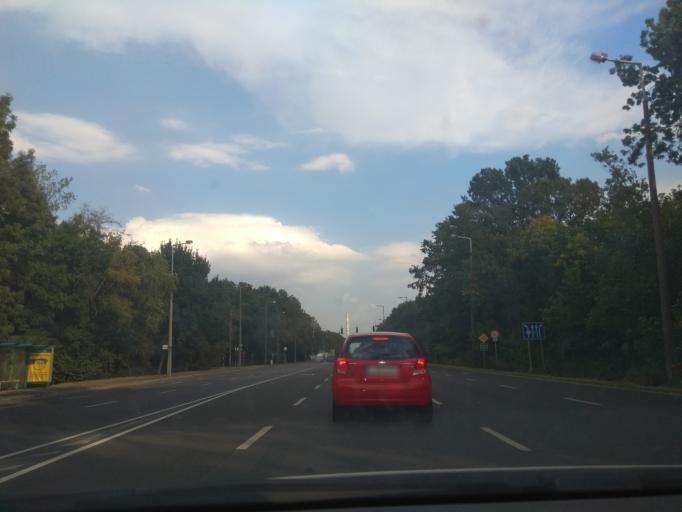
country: HU
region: Borsod-Abauj-Zemplen
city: Sajooeroes
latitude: 47.9270
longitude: 21.0369
